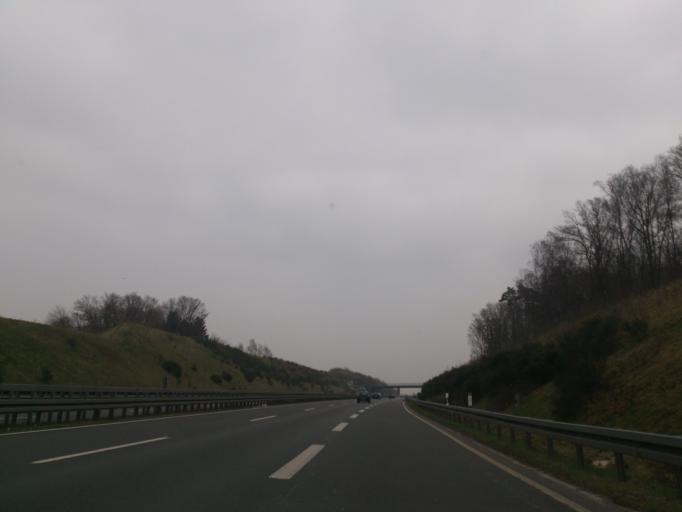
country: DE
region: North Rhine-Westphalia
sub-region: Regierungsbezirk Dusseldorf
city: Bruggen
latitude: 51.2103
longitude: 6.1371
